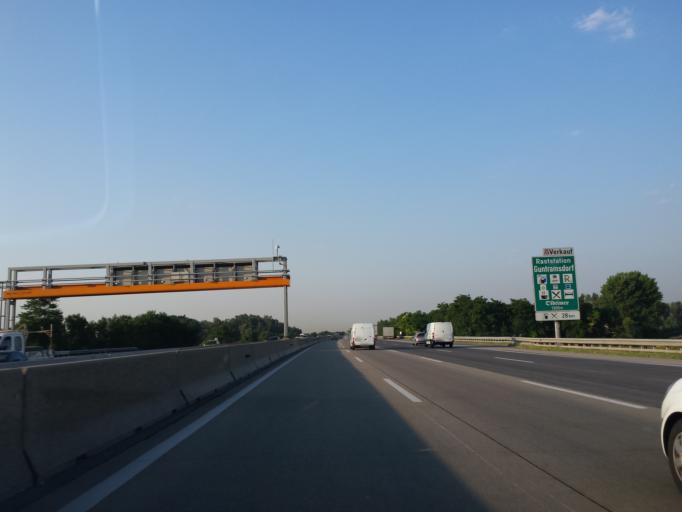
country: AT
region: Lower Austria
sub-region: Politischer Bezirk Modling
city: Laxenburg
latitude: 48.0463
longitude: 16.3419
